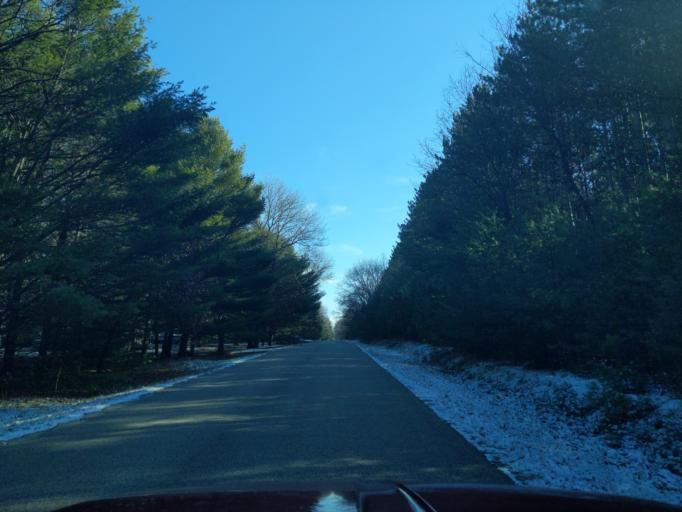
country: US
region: Wisconsin
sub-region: Waushara County
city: Silver Lake
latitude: 44.1052
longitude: -89.1768
